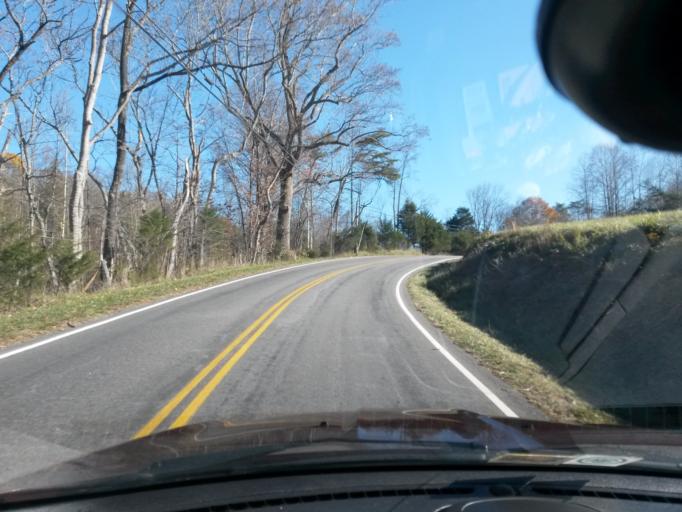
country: US
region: Virginia
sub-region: Botetourt County
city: Buchanan
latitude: 37.6434
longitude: -79.7688
